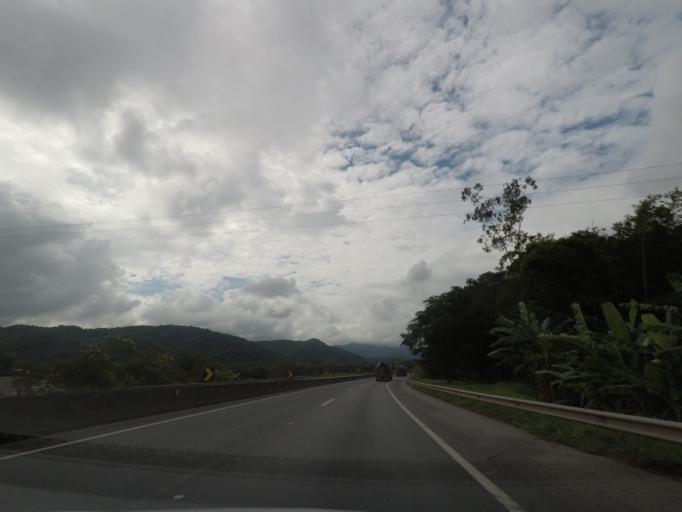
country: BR
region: Sao Paulo
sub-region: Miracatu
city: Miracatu
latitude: -24.1857
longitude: -47.3592
